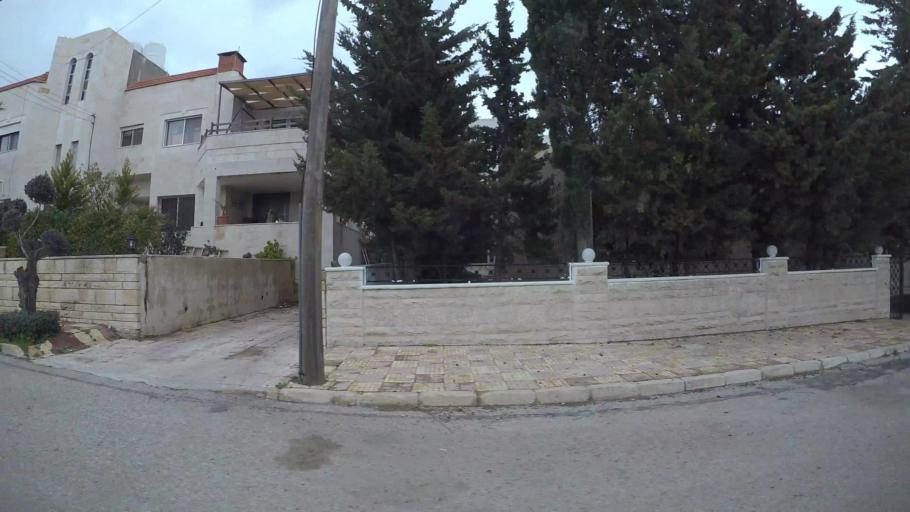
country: JO
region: Amman
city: Wadi as Sir
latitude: 31.9918
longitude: 35.8316
